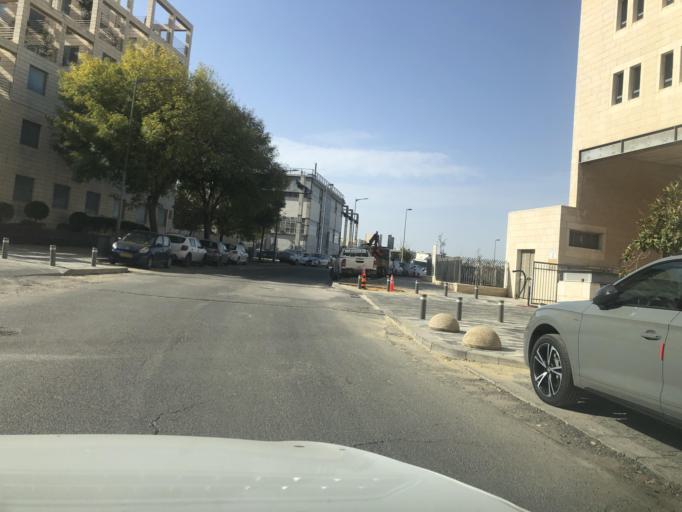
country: IL
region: Jerusalem
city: West Jerusalem
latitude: 31.8042
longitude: 35.2111
